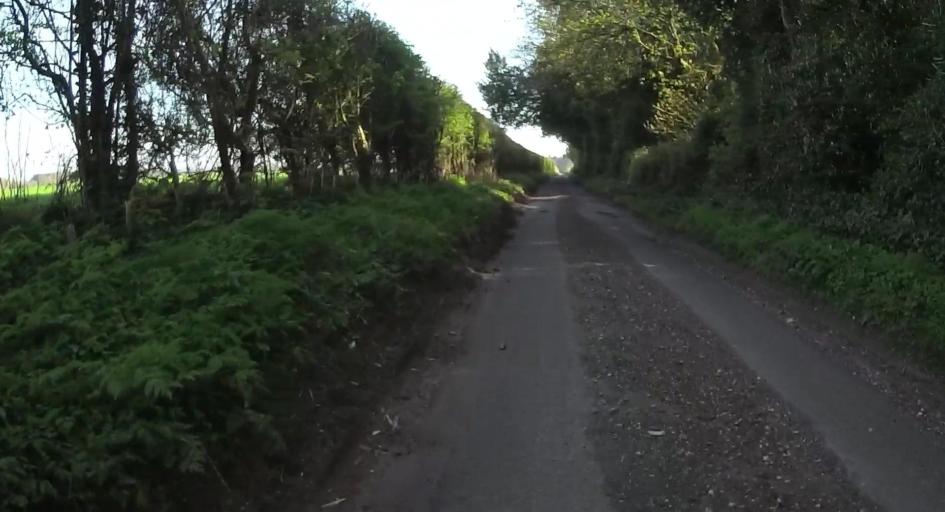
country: GB
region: England
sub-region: Hampshire
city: Highclere
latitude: 51.2621
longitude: -1.3694
